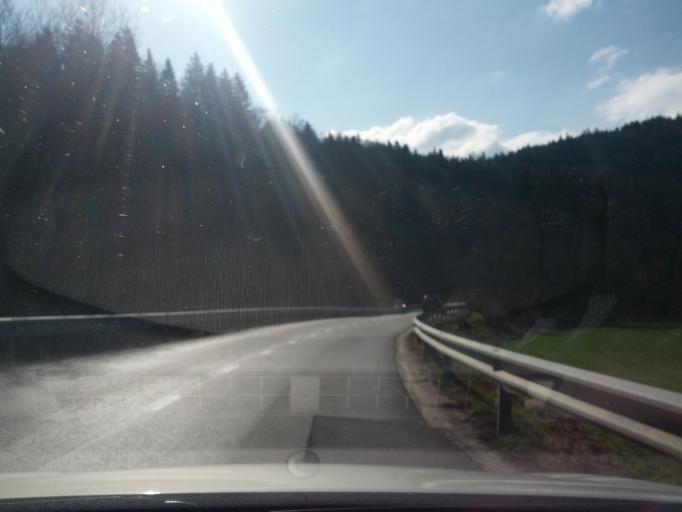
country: SI
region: Litija
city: Litija
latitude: 46.0877
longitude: 14.8369
